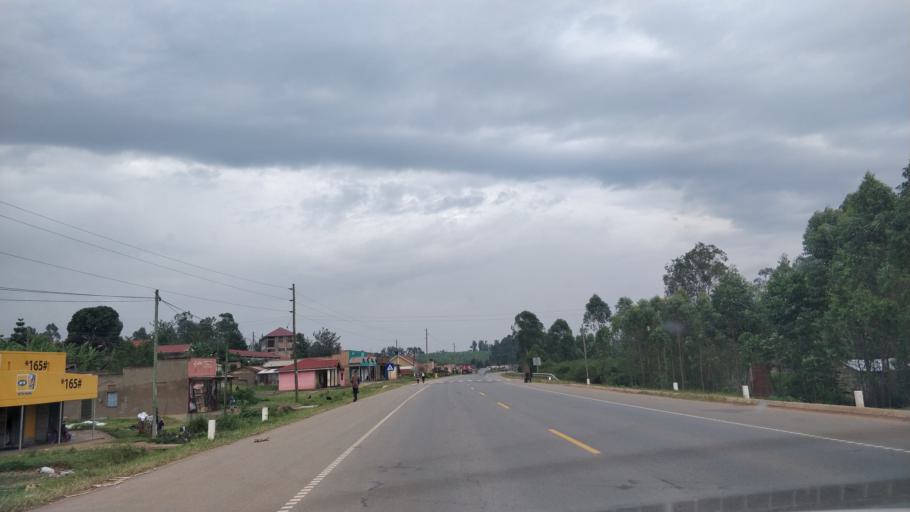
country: UG
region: Western Region
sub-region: Sheema District
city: Kibingo
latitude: -0.6605
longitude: 30.4563
